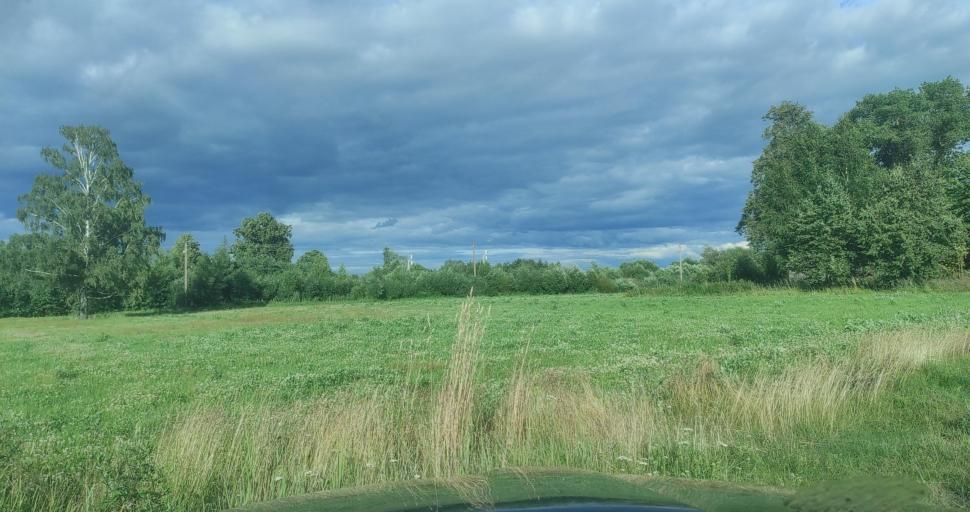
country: LV
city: Tireli
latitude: 56.7071
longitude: 23.4542
